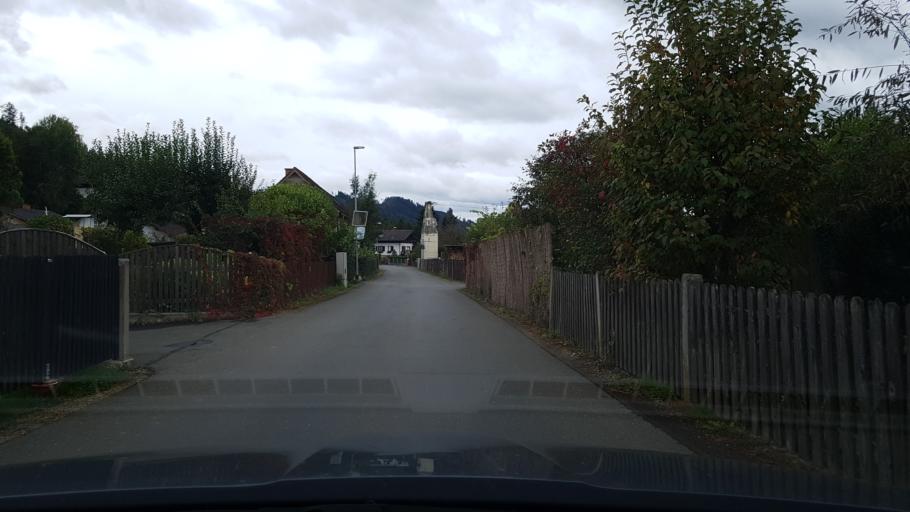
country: AT
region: Styria
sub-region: Politischer Bezirk Bruck-Muerzzuschlag
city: Allerheiligen im Muerztal
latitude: 47.4776
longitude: 15.4070
